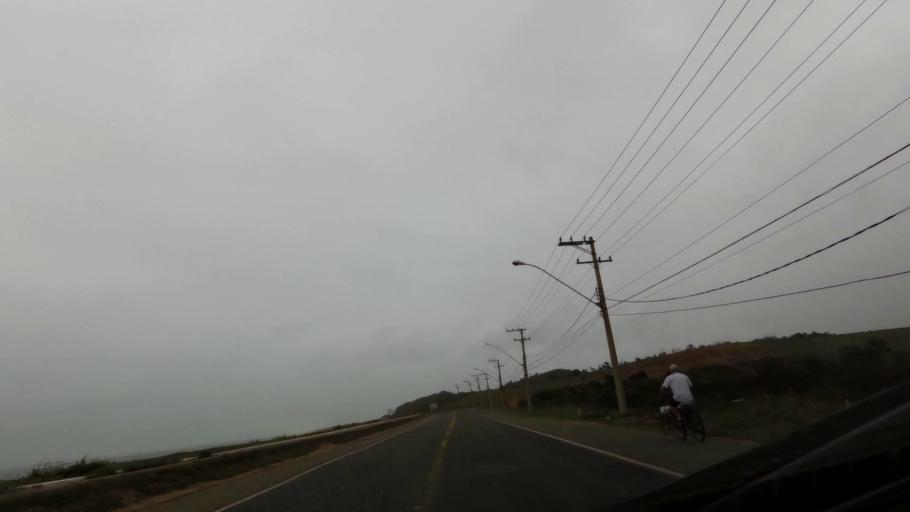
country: BR
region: Espirito Santo
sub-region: Guarapari
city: Guarapari
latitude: -20.6965
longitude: -40.5137
